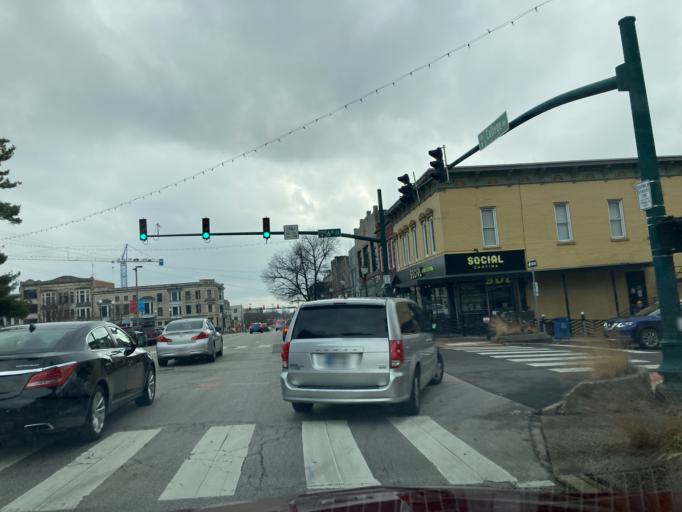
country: US
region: Indiana
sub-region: Monroe County
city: Bloomington
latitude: 39.1678
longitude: -86.5349
